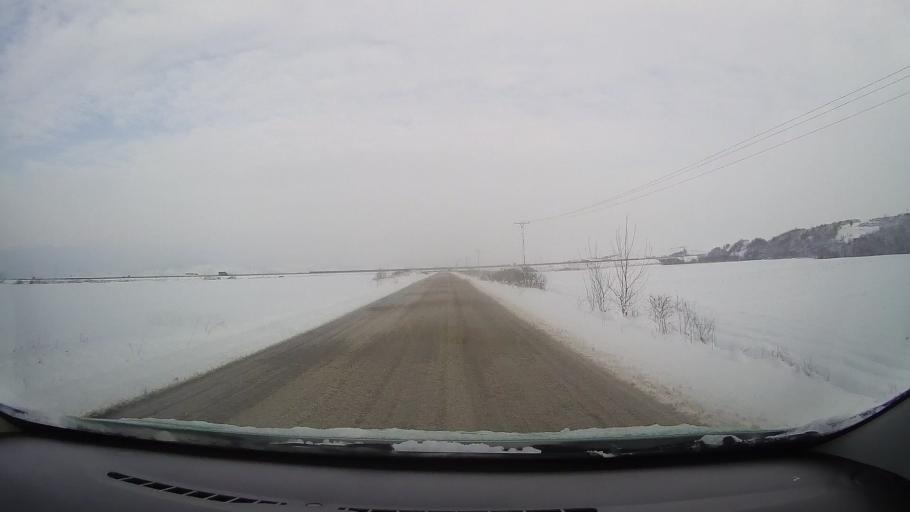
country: RO
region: Alba
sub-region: Comuna Pianu
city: Pianu de Jos
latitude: 45.9620
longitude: 23.4768
